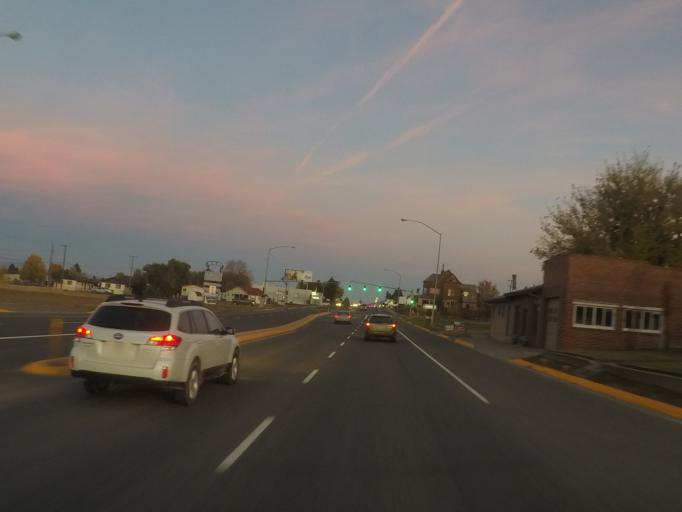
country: US
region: Montana
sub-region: Lewis and Clark County
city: Helena
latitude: 46.6068
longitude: -112.0684
